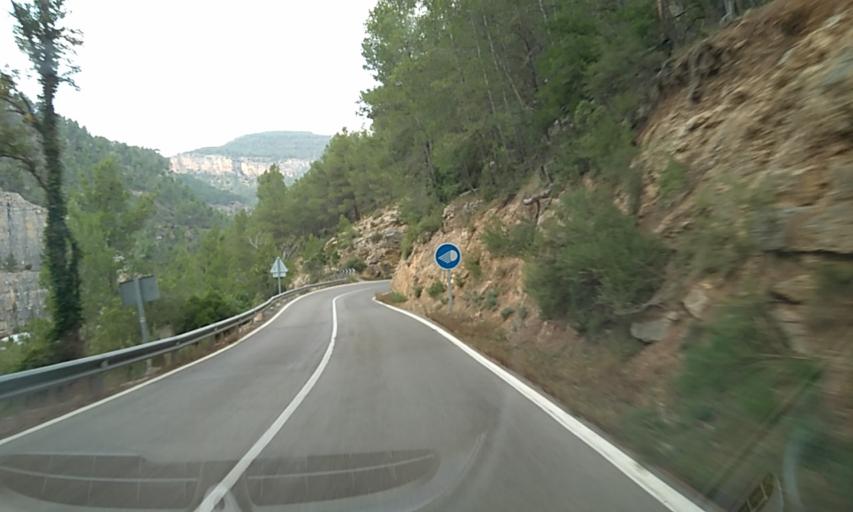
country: ES
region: Valencia
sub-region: Provincia de Castello
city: Montanejos
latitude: 40.0845
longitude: -0.5424
